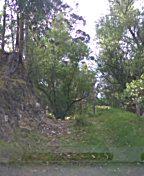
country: CO
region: Boyaca
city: Duitama
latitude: 5.8247
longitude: -73.0817
